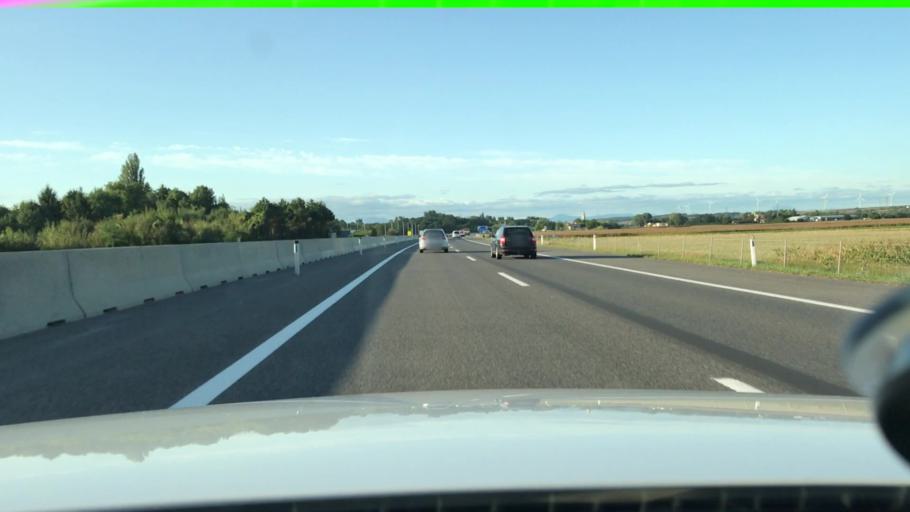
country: AT
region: Lower Austria
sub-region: Politischer Bezirk Sankt Polten
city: Traismauer
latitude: 48.3163
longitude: 15.7179
